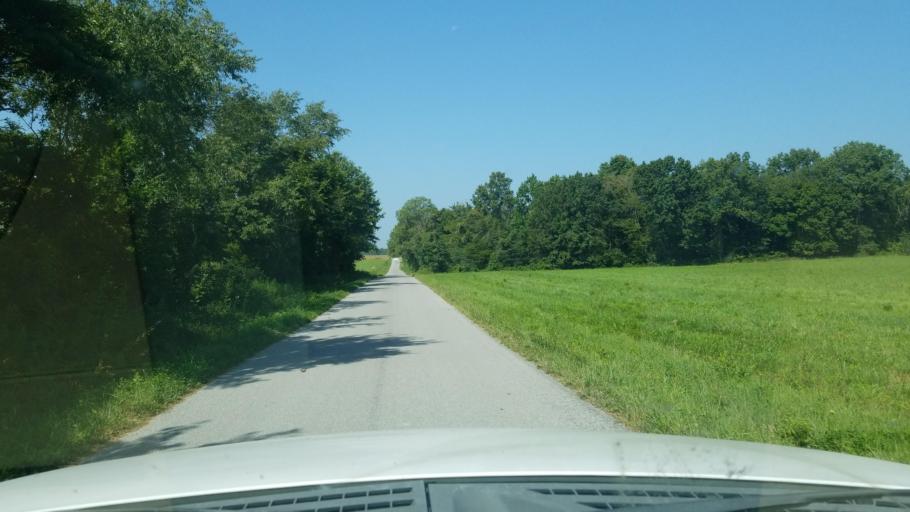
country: US
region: Illinois
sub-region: Saline County
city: Harrisburg
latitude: 37.8922
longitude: -88.6637
